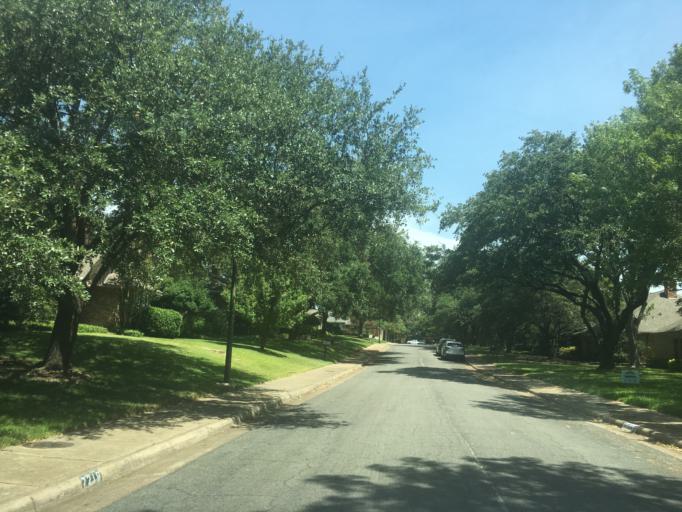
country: US
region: Texas
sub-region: Dallas County
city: Richardson
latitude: 32.8809
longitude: -96.7373
